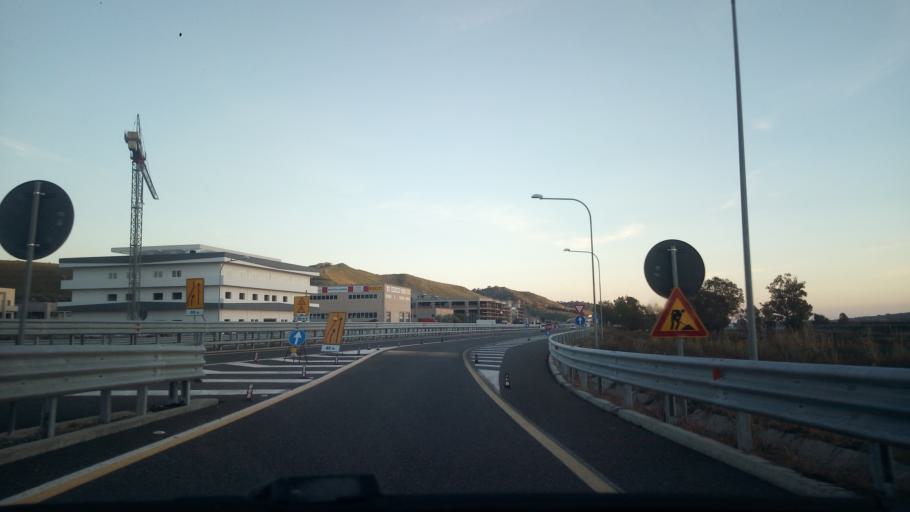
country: IT
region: Calabria
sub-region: Provincia di Catanzaro
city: Catanzaro
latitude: 38.8491
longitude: 16.5794
